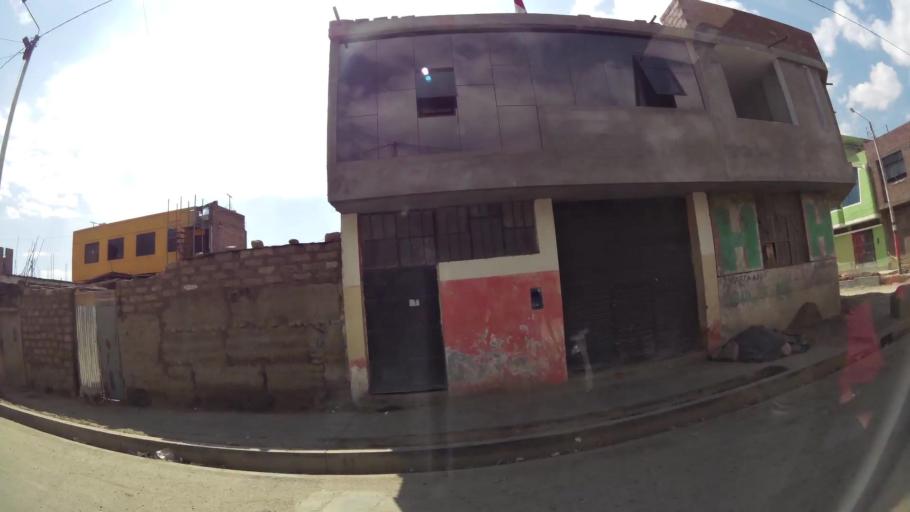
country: PE
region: Junin
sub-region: Provincia de Huancayo
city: Huancayo
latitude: -12.0929
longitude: -75.2033
